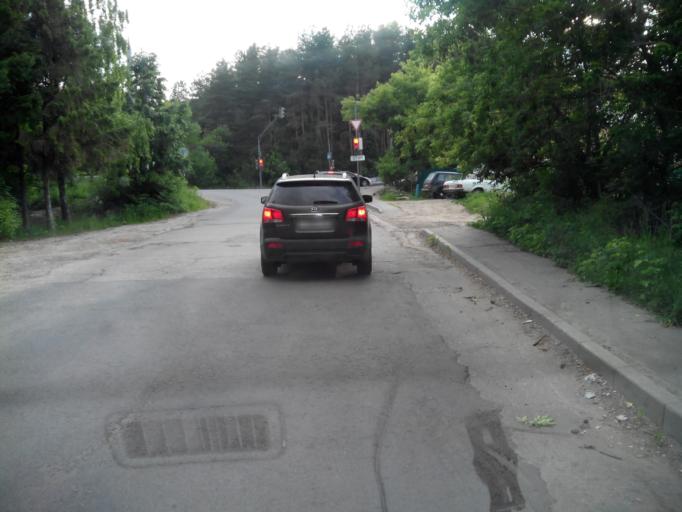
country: RU
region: Penza
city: Penza
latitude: 53.1980
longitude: 44.9643
